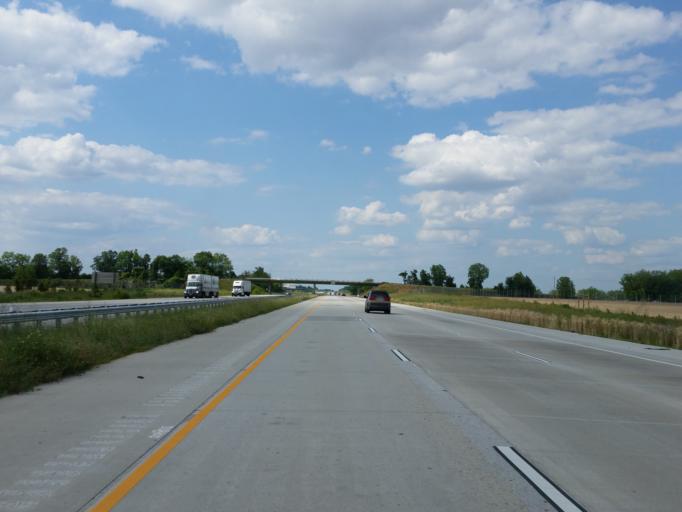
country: US
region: Georgia
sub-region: Dooly County
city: Vienna
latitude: 32.1409
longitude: -83.7578
